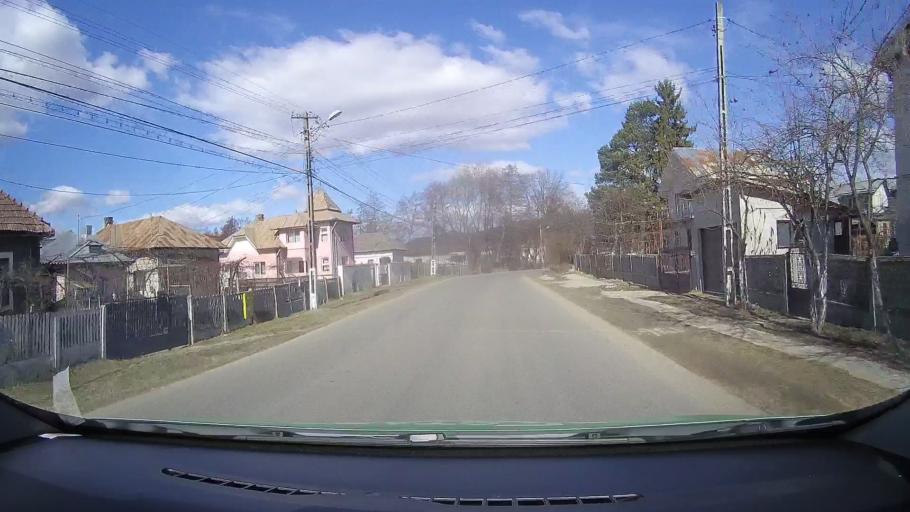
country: RO
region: Dambovita
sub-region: Comuna Vulcana-Pandele
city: Gura Vulcanei
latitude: 45.0280
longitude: 25.3952
